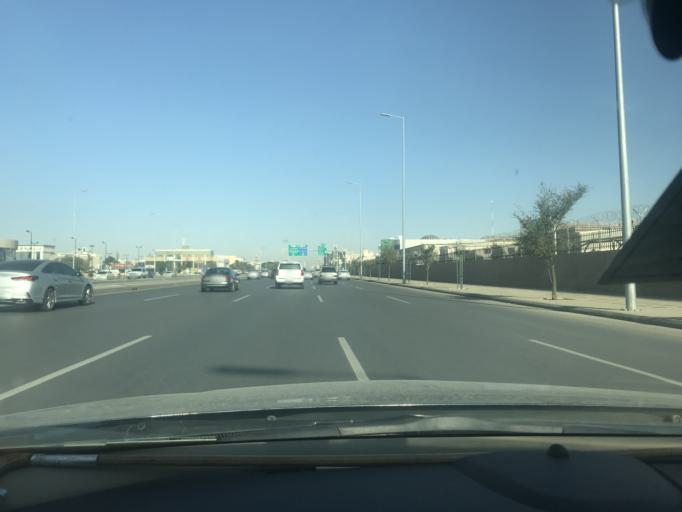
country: SA
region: Ar Riyad
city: Riyadh
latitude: 24.7435
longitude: 46.6819
